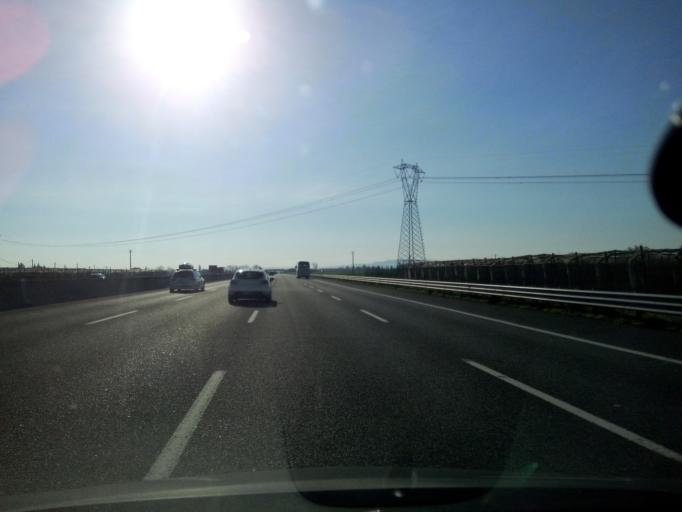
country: IT
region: Emilia-Romagna
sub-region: Provincia di Modena
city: Piumazzo
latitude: 44.5575
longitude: 11.0628
